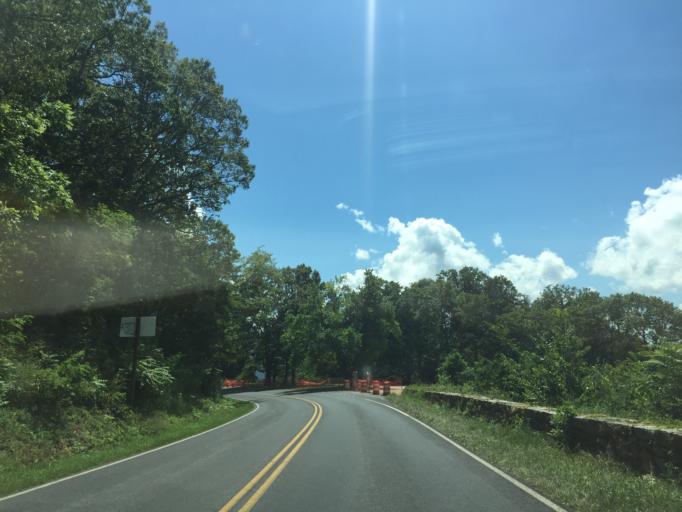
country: US
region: Virginia
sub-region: Warren County
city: Front Royal
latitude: 38.8432
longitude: -78.2073
